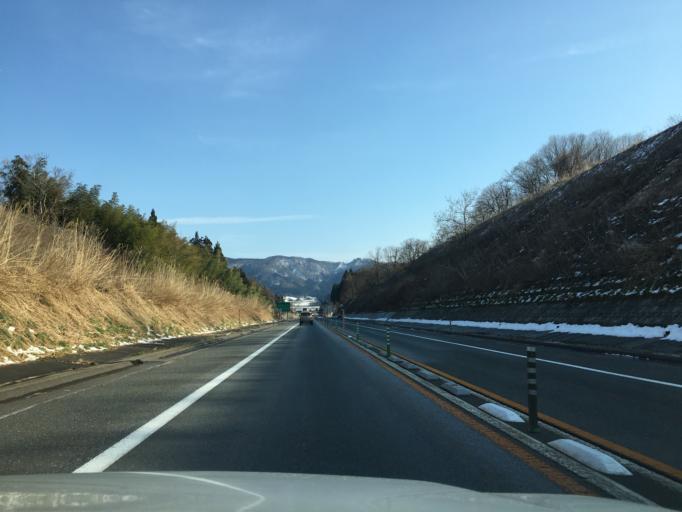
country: JP
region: Yamagata
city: Tsuruoka
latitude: 38.6298
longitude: 139.8365
